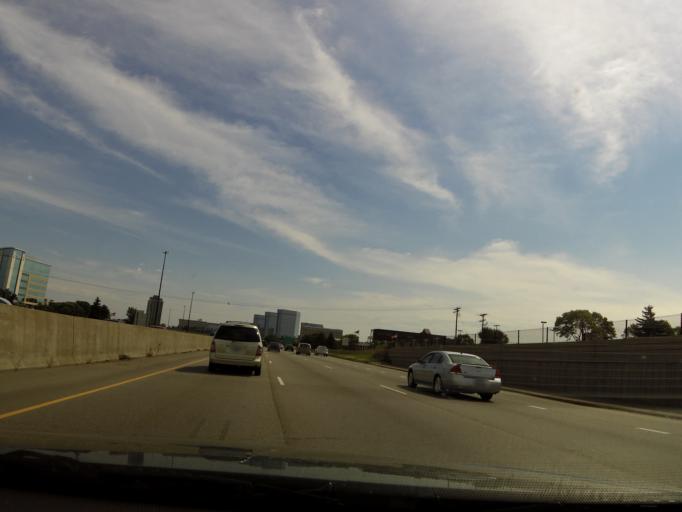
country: US
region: Minnesota
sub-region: Hennepin County
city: Edina
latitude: 44.8581
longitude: -93.3408
